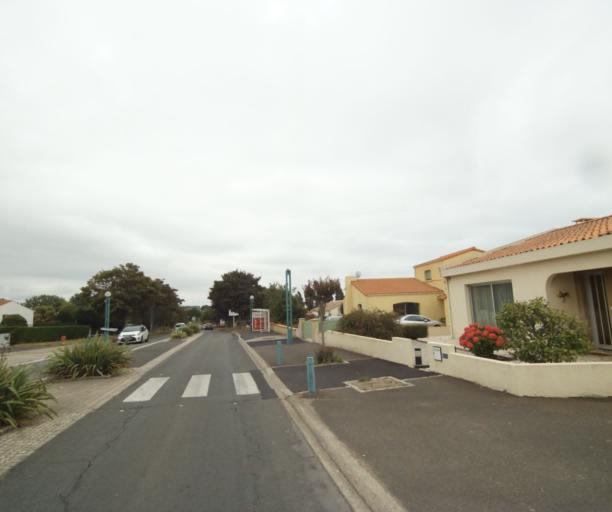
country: FR
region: Pays de la Loire
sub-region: Departement de la Vendee
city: Chateau-d'Olonne
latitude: 46.4901
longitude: -1.7525
